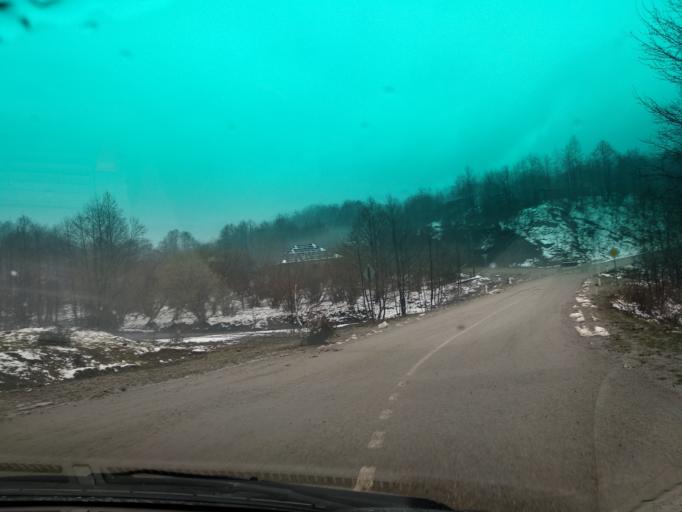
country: RU
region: Krasnodarskiy
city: Khadyzhensk
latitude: 44.2091
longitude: 39.4318
